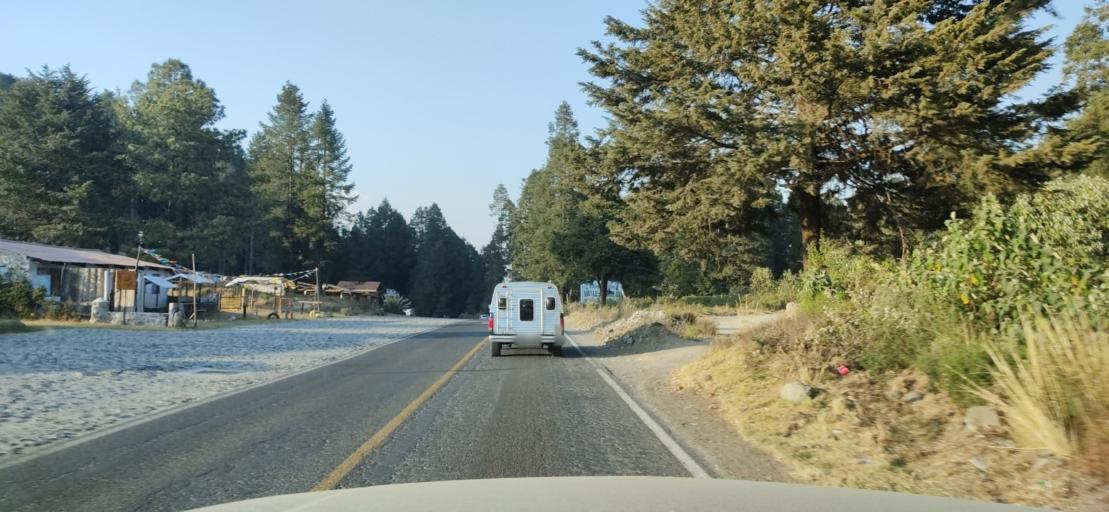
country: MX
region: Mexico
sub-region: Ocoyoacac
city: San Jeronimo Acazulco
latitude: 19.2714
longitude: -99.3760
